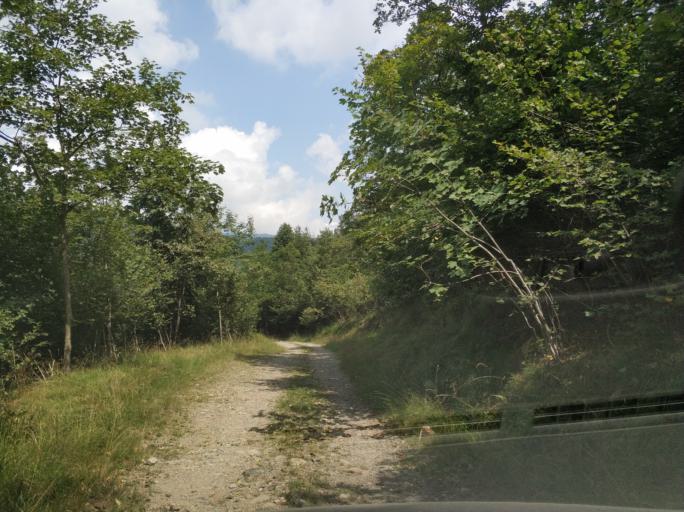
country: IT
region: Piedmont
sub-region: Provincia di Torino
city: Viu
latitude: 45.2059
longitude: 7.3940
